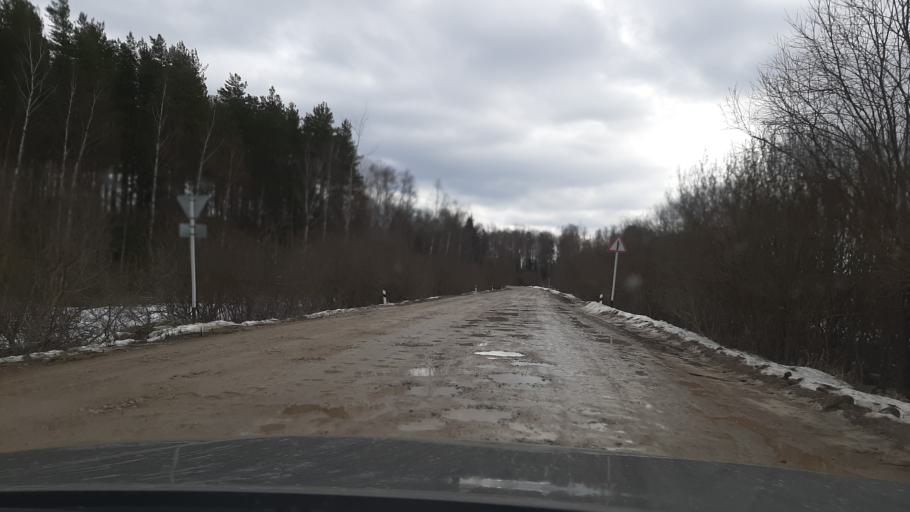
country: RU
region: Ivanovo
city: Teykovo
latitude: 56.8874
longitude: 40.6177
